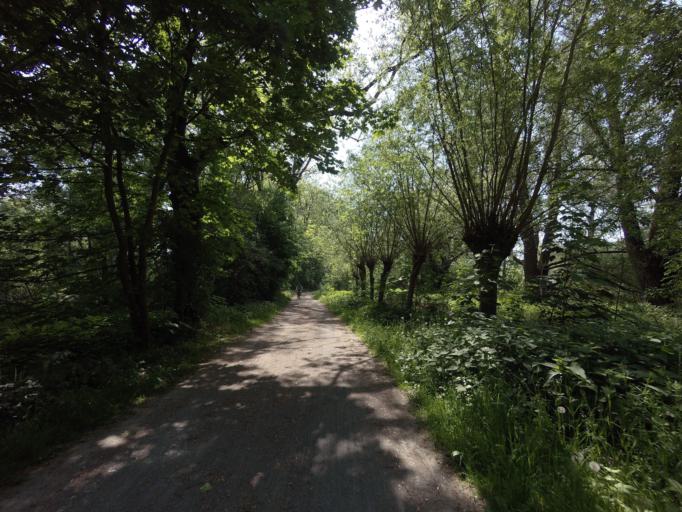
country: DE
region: Lower Saxony
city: Braunschweig
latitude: 52.2732
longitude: 10.5625
